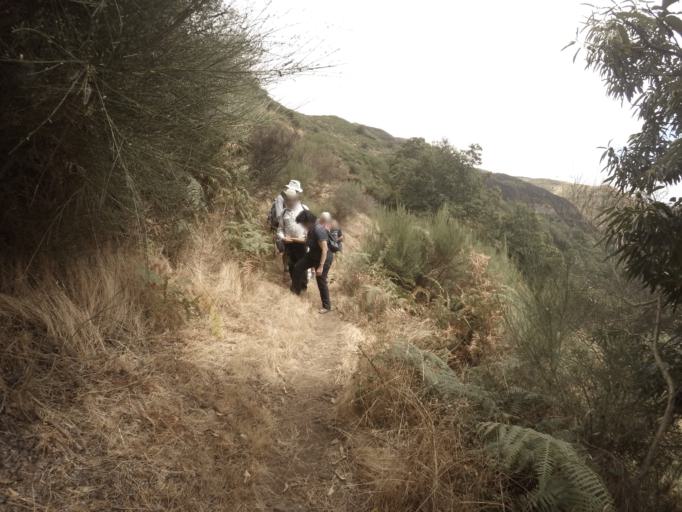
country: PT
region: Madeira
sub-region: Camara de Lobos
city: Curral das Freiras
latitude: 32.7080
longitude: -17.0090
